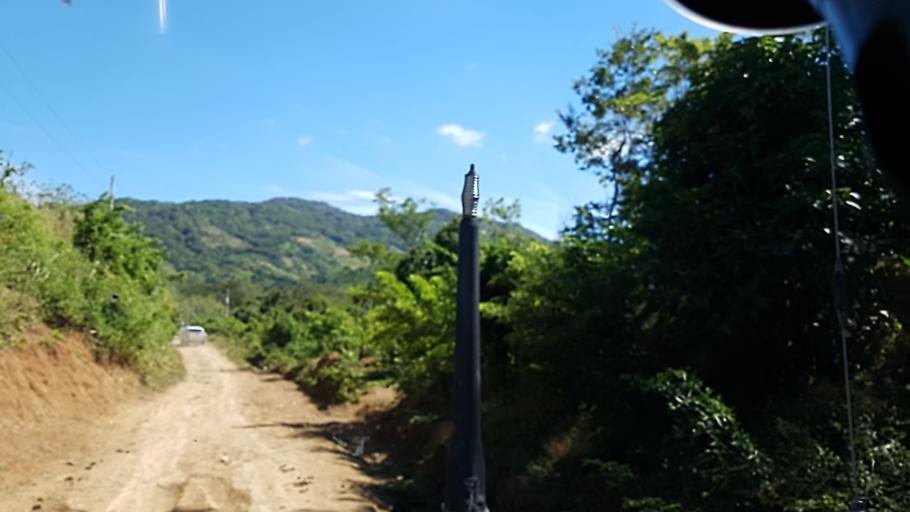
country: NI
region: Carazo
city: Santa Teresa
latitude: 11.6697
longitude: -86.1783
